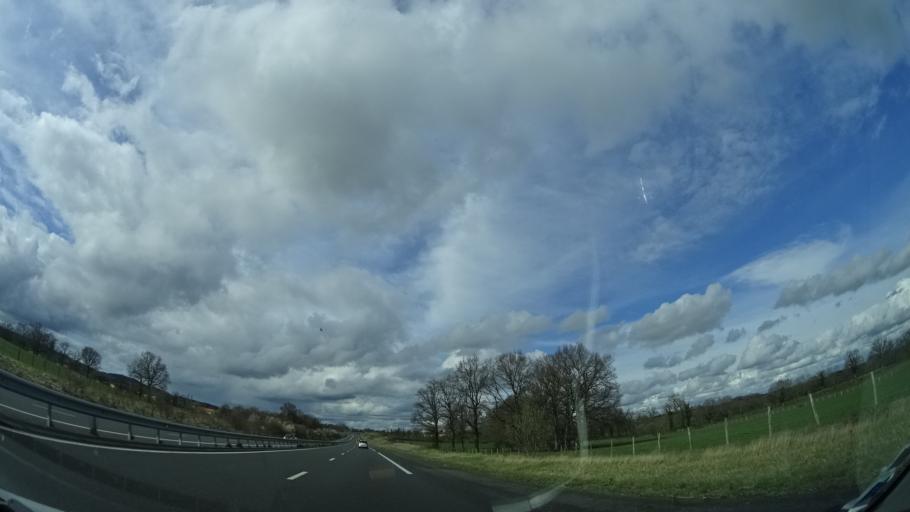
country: FR
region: Rhone-Alpes
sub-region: Departement de la Loire
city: La Pacaudiere
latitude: 46.1640
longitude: 3.8884
